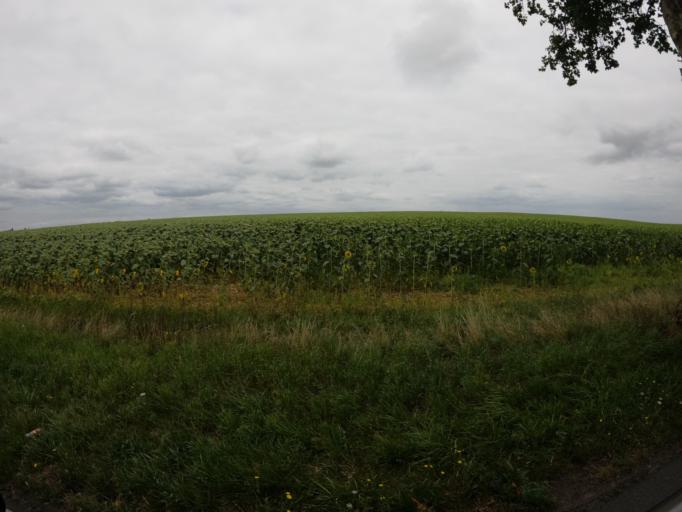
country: FR
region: Pays de la Loire
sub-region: Departement de la Vendee
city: Saint-Martin-sous-Mouzeuil
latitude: 46.5209
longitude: -0.9843
